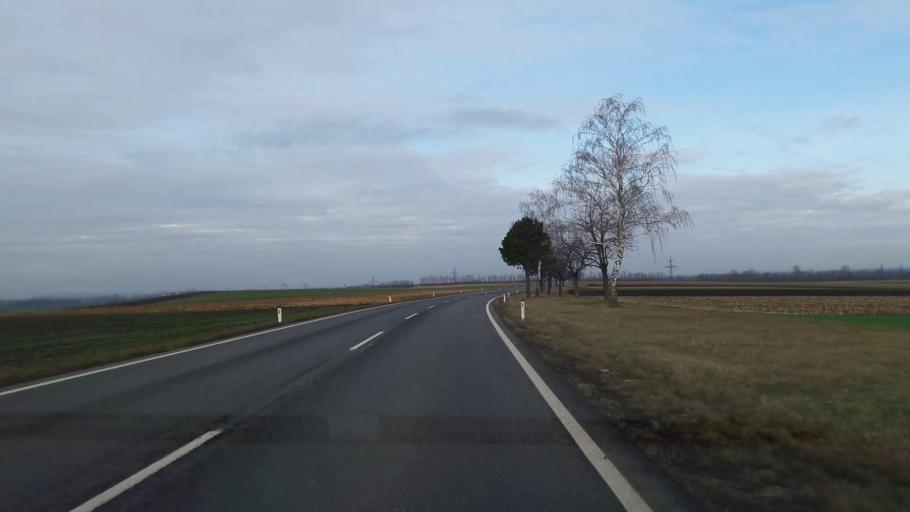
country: AT
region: Lower Austria
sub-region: Politischer Bezirk Mistelbach
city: Staatz
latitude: 48.6963
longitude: 16.4451
